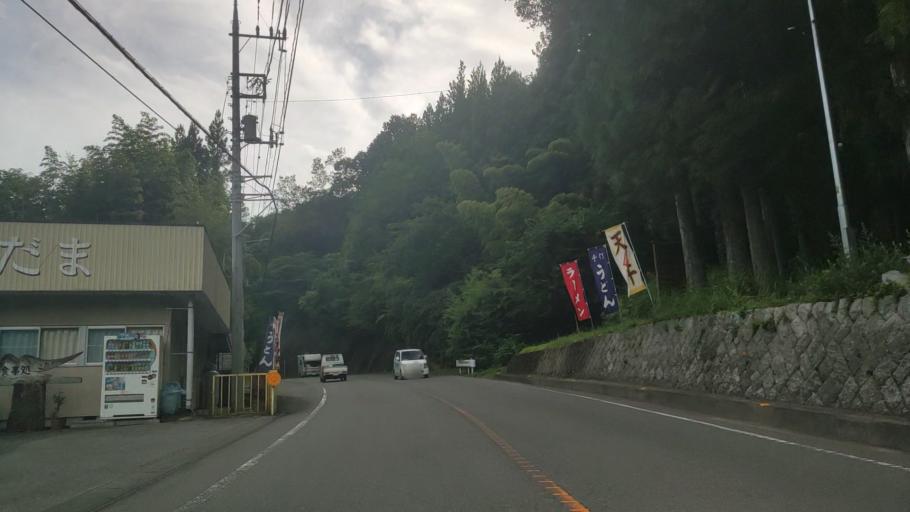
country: JP
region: Gunma
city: Omamacho-omama
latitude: 36.5732
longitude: 139.3796
